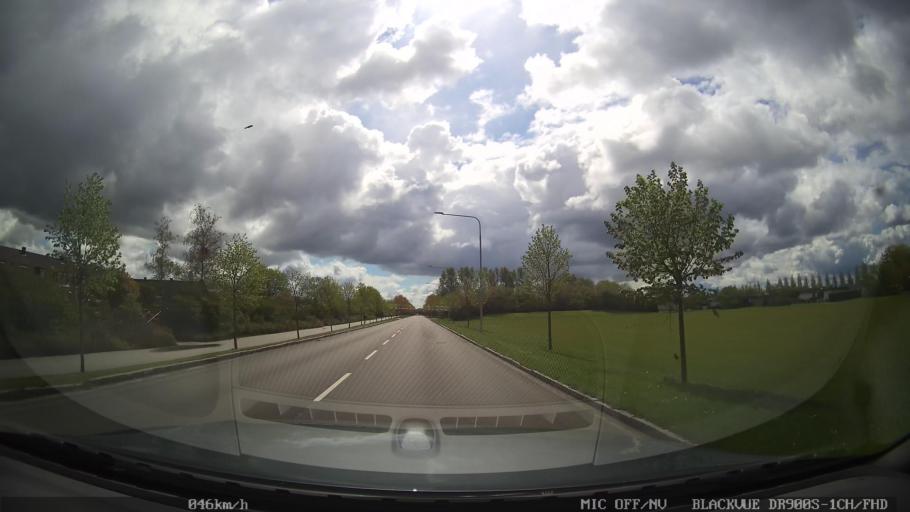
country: SE
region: Skane
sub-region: Landskrona
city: Landskrona
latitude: 55.8963
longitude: 12.8143
